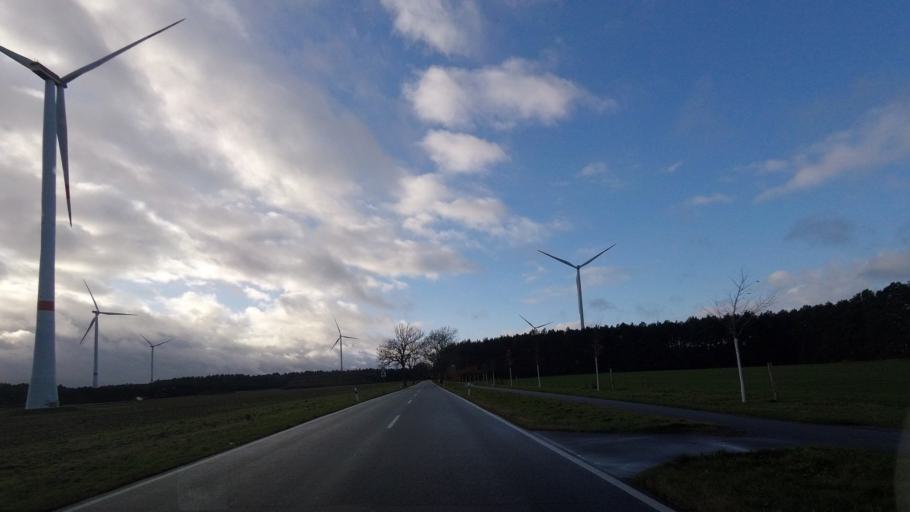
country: DE
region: Brandenburg
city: Linthe
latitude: 52.0959
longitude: 12.7985
